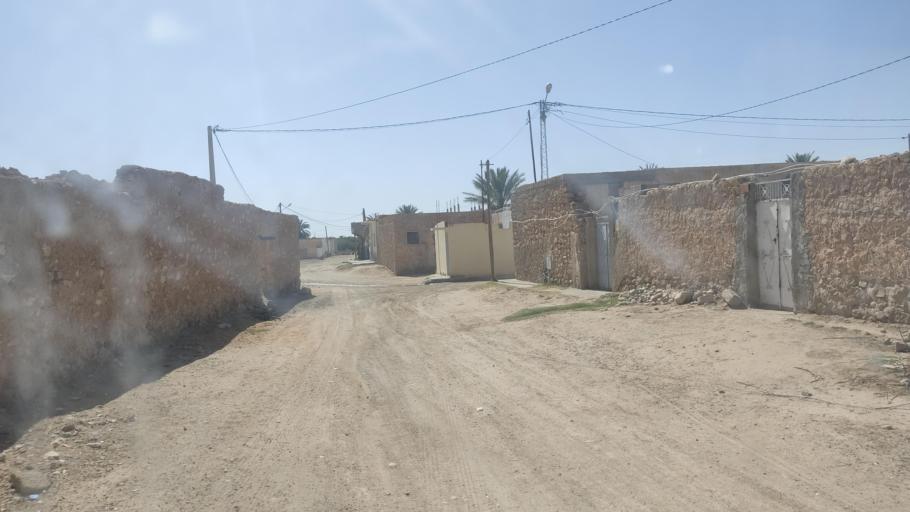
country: TN
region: Gafsa
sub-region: Gafsa Municipality
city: Gafsa
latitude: 34.3338
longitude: 8.9205
